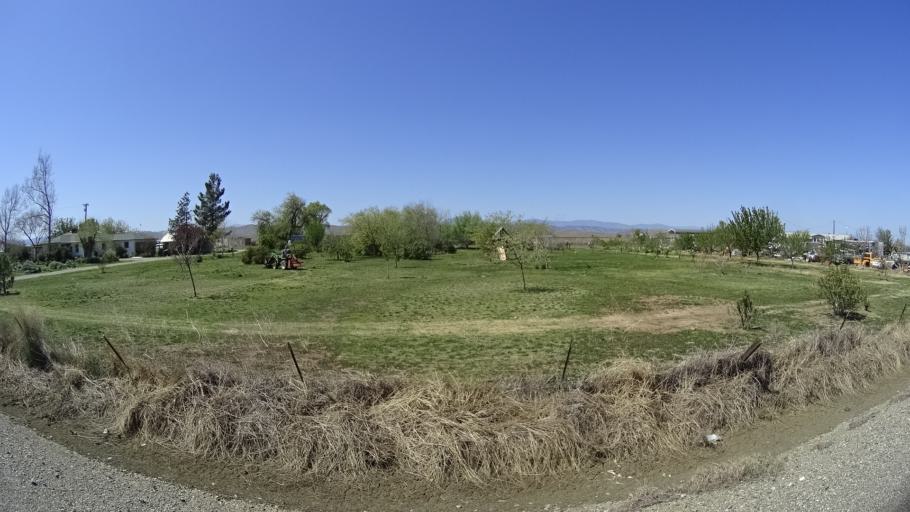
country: US
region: California
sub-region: Glenn County
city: Willows
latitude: 39.4109
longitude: -122.2484
